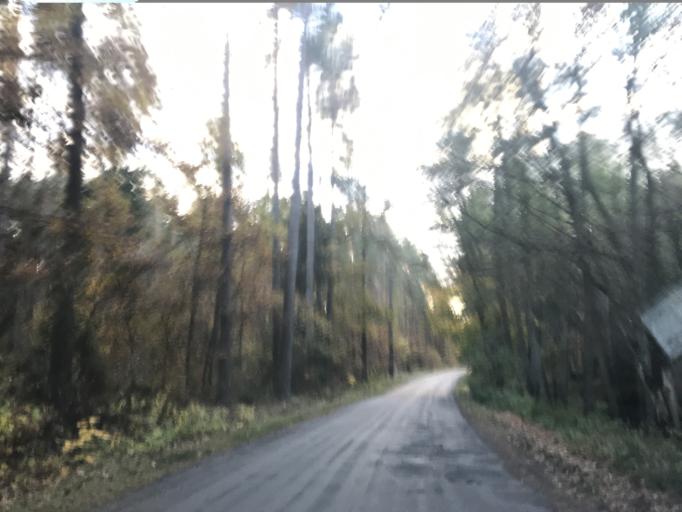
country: PL
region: Warmian-Masurian Voivodeship
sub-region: Powiat dzialdowski
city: Lidzbark
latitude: 53.2305
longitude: 19.7961
